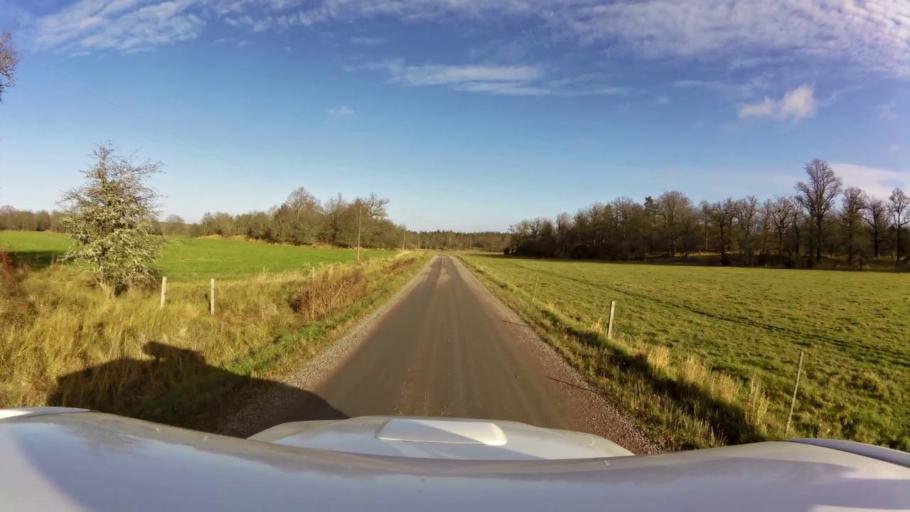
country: SE
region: OEstergoetland
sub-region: Linkopings Kommun
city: Linkoping
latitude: 58.3687
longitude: 15.6111
